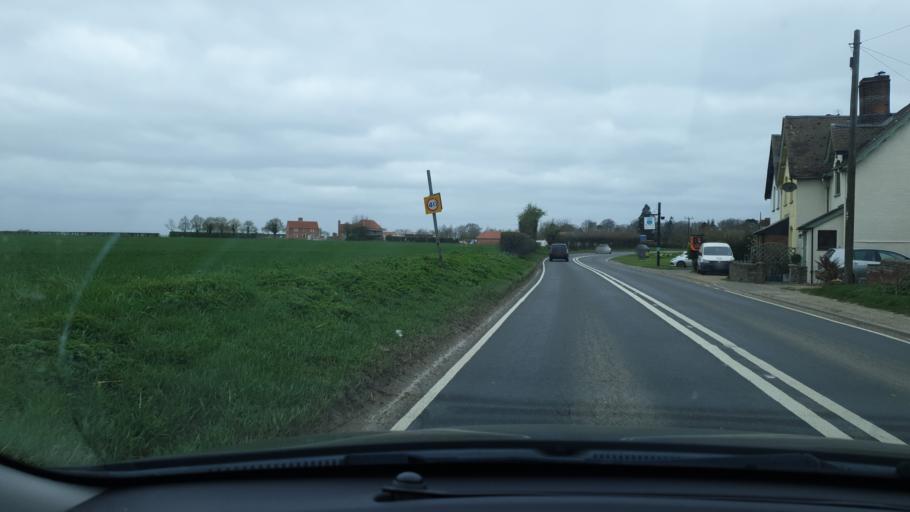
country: GB
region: England
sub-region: Essex
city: Great Horkesley
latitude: 51.9512
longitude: 0.8730
